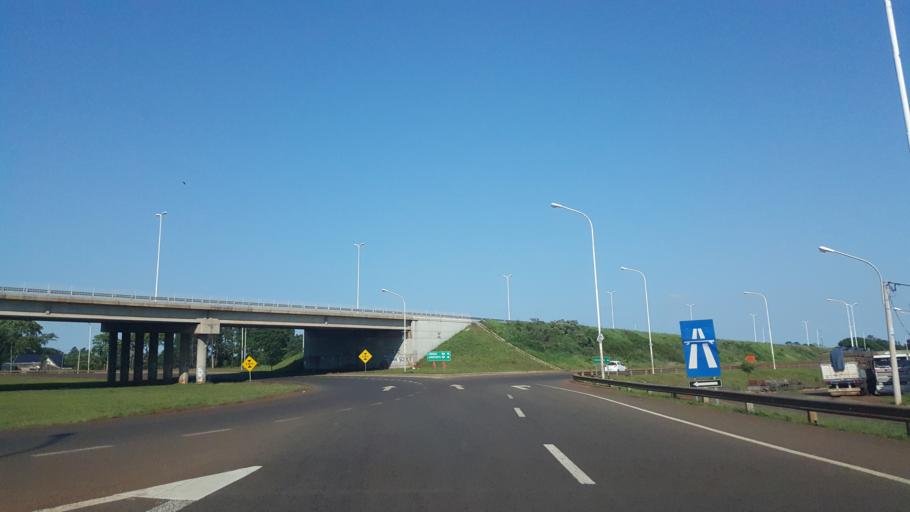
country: AR
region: Misiones
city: Garupa
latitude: -27.4534
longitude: -55.8615
